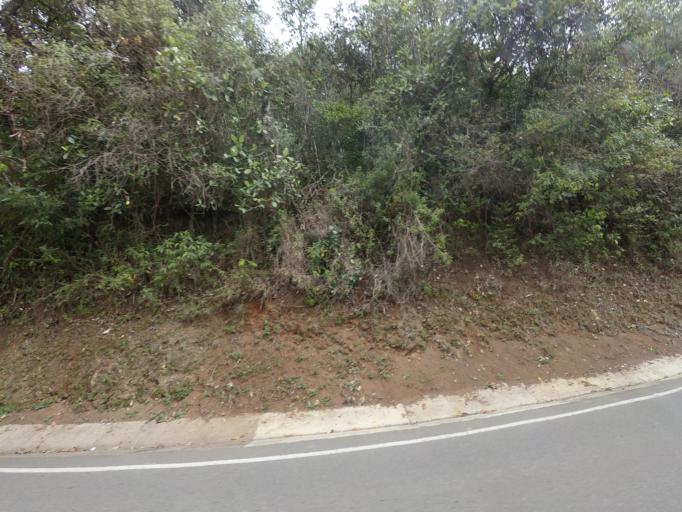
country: CO
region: Huila
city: San Agustin
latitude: 1.8886
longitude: -76.2925
